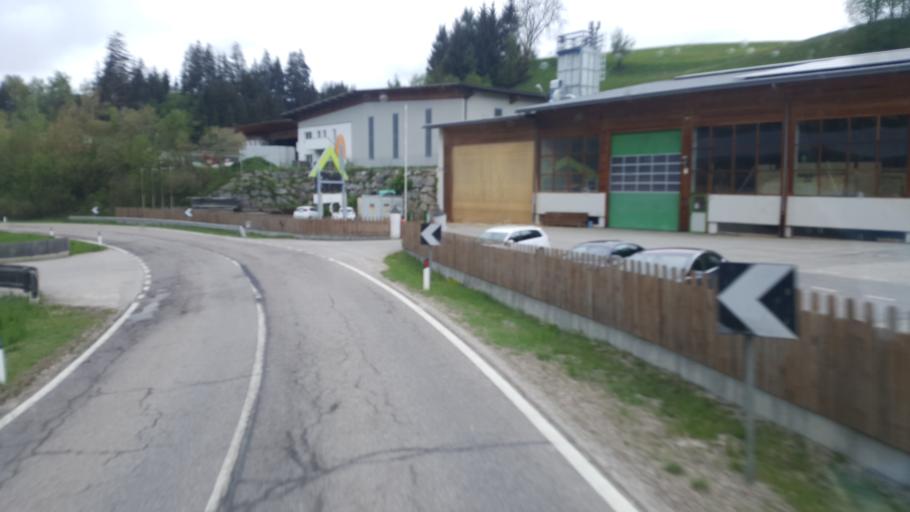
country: IT
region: Trentino-Alto Adige
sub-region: Bolzano
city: Monguelfo
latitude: 46.7668
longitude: 12.1212
